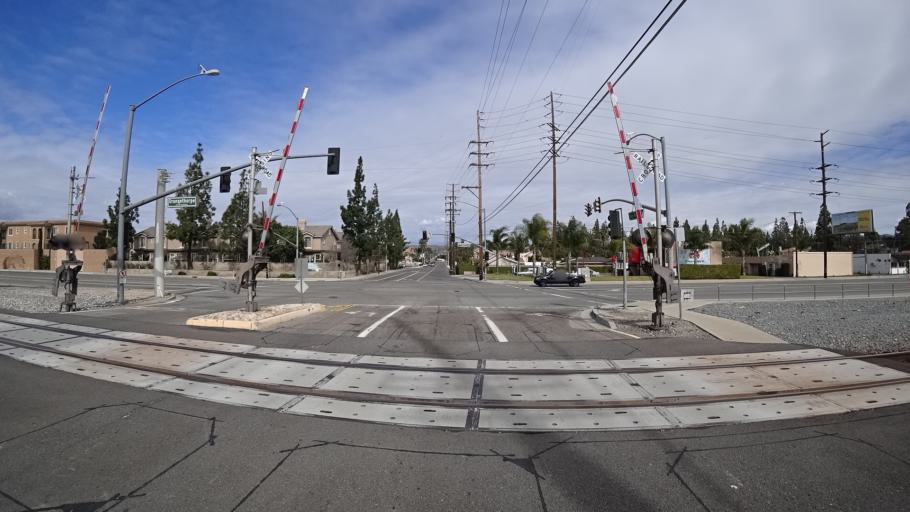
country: US
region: California
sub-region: Orange County
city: Yorba Linda
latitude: 33.8679
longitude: -117.8313
